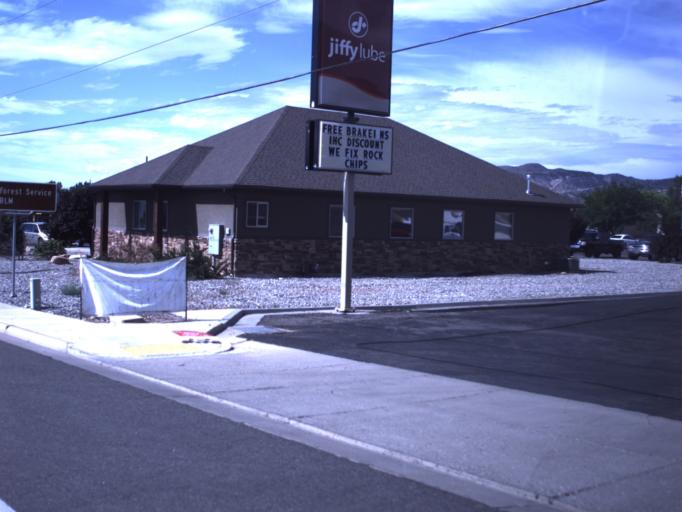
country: US
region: Utah
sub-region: Sevier County
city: Richfield
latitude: 38.7817
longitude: -112.0849
